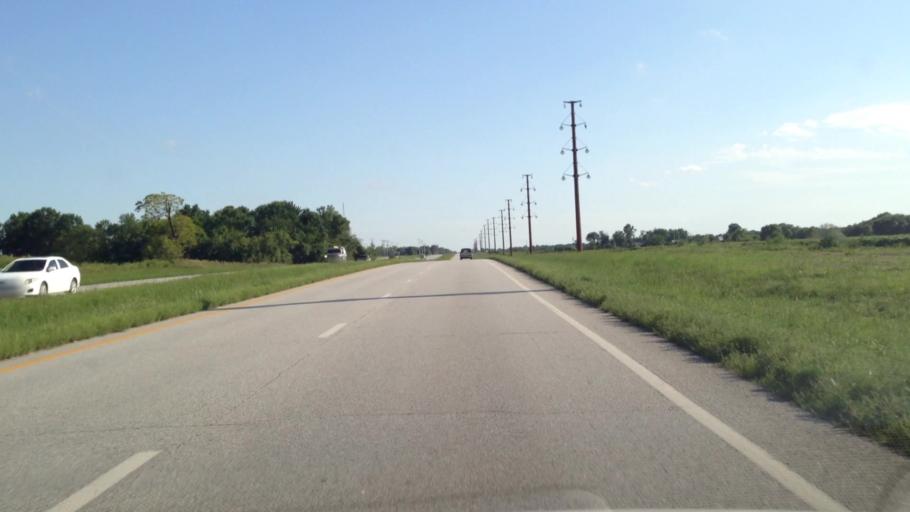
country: US
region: Kansas
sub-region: Crawford County
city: Frontenac
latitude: 37.4951
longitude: -94.7053
